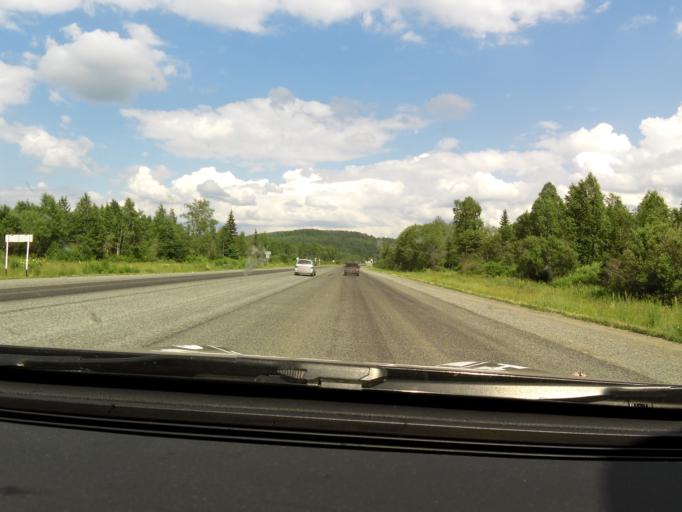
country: RU
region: Sverdlovsk
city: Arti
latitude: 56.7934
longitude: 58.6118
